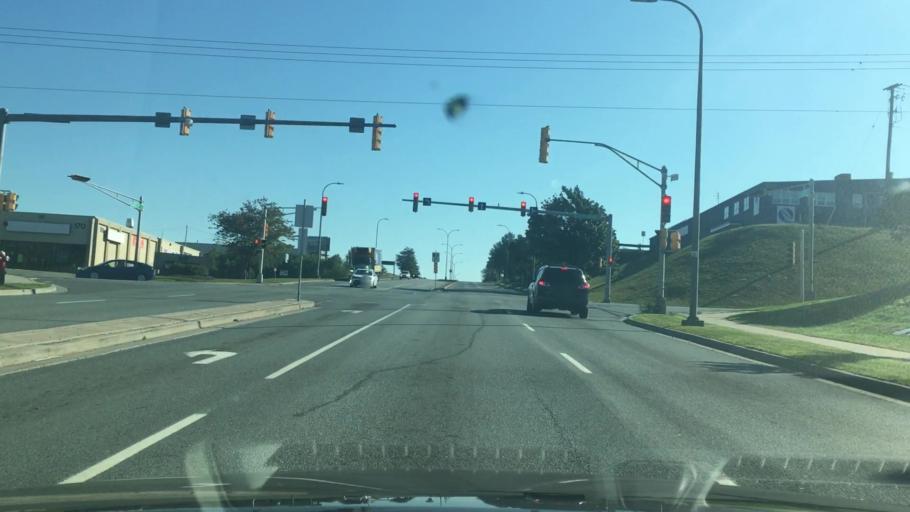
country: CA
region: Nova Scotia
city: Dartmouth
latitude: 44.7113
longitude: -63.6005
